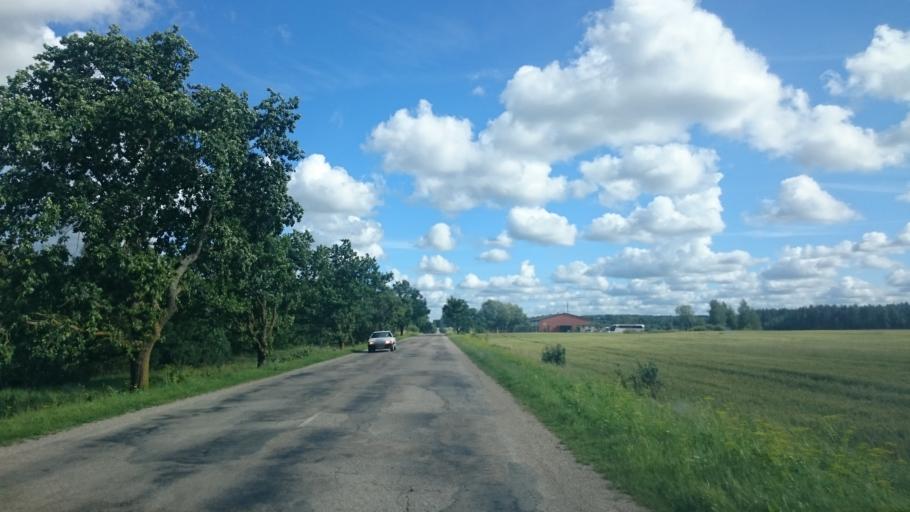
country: LV
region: Aizpute
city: Aizpute
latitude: 56.7010
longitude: 21.6285
